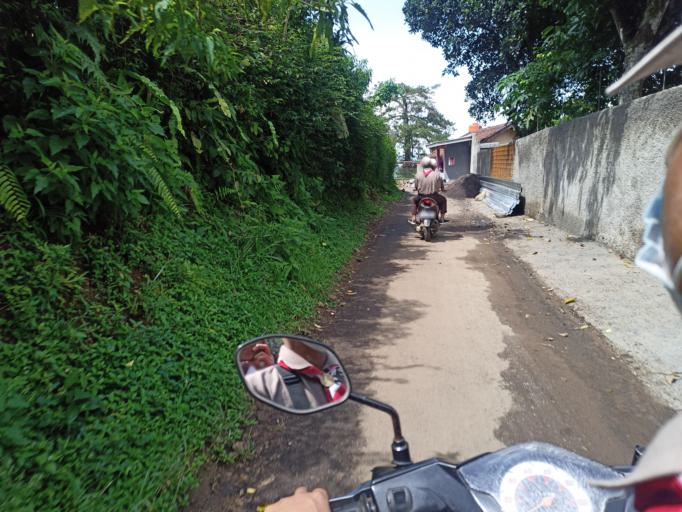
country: ID
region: West Java
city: Caringin
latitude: -6.6439
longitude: 106.9096
